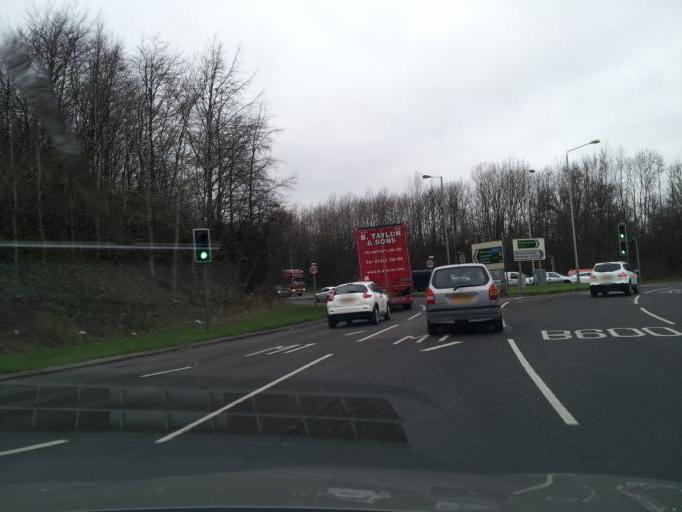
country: GB
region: England
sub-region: Nottinghamshire
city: Kimberley
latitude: 52.9901
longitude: -1.2247
